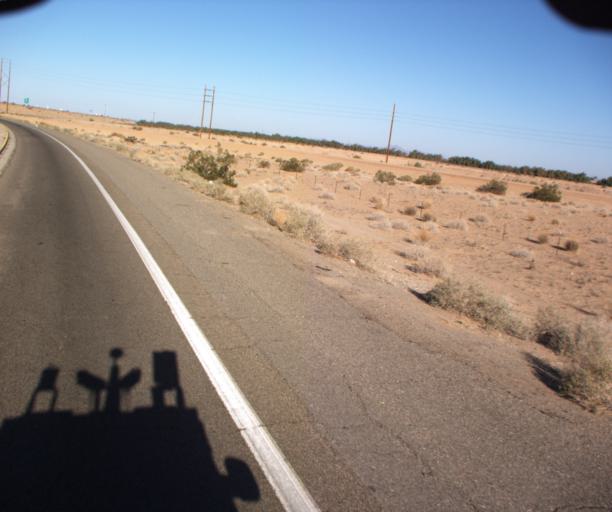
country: US
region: Arizona
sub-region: Yuma County
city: Fortuna Foothills
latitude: 32.6744
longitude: -114.4875
